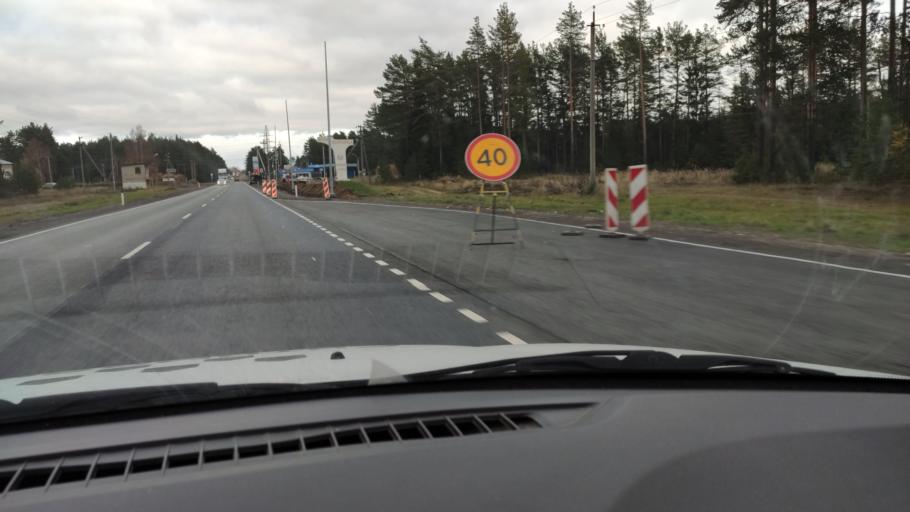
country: RU
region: Kirov
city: Belaya Kholunitsa
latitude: 58.8448
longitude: 50.8124
